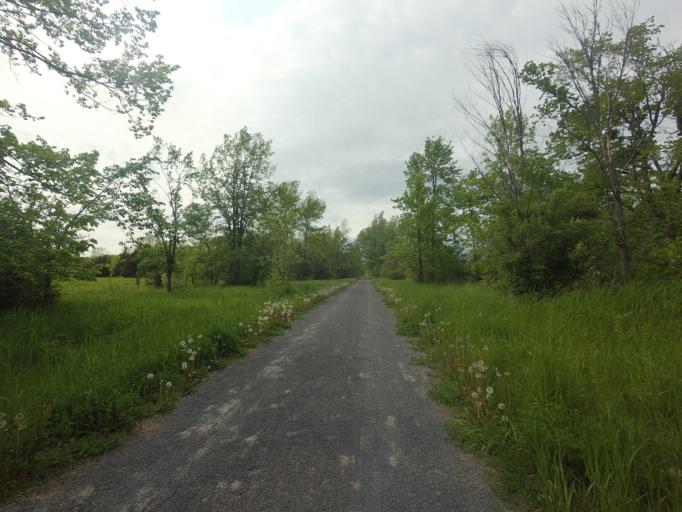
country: CA
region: Ontario
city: Kingston
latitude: 44.3467
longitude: -76.6078
